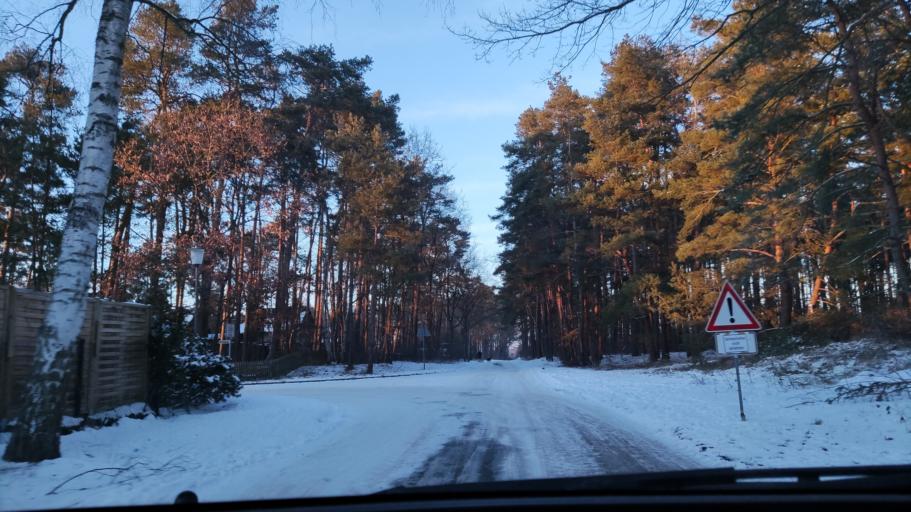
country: DE
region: Lower Saxony
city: Bleckede
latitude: 53.2927
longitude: 10.6914
